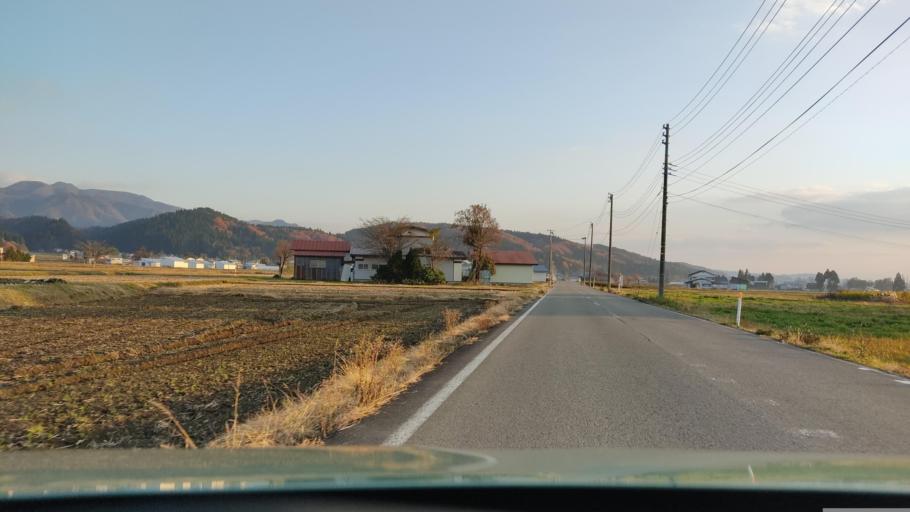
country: JP
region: Akita
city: Omagari
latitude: 39.4598
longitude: 140.5842
